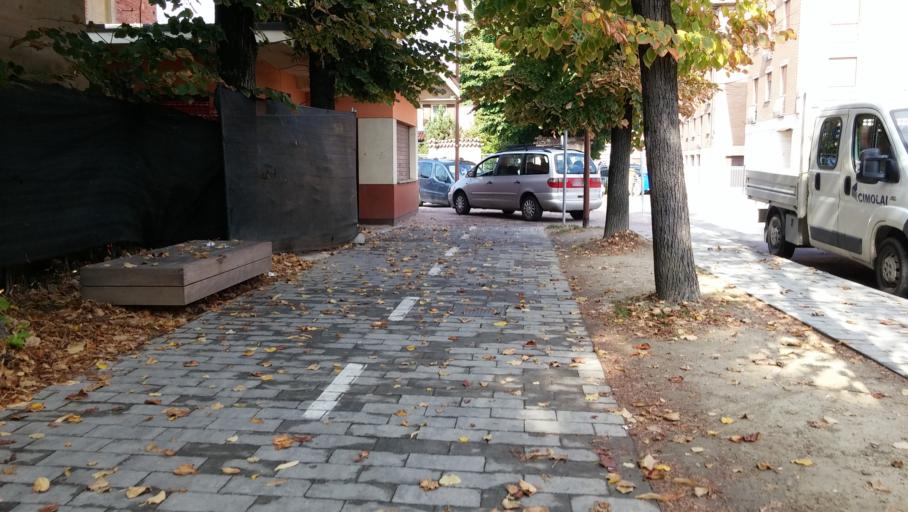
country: IT
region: Emilia-Romagna
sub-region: Provincia di Ferrara
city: Cento
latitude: 44.7293
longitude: 11.2859
